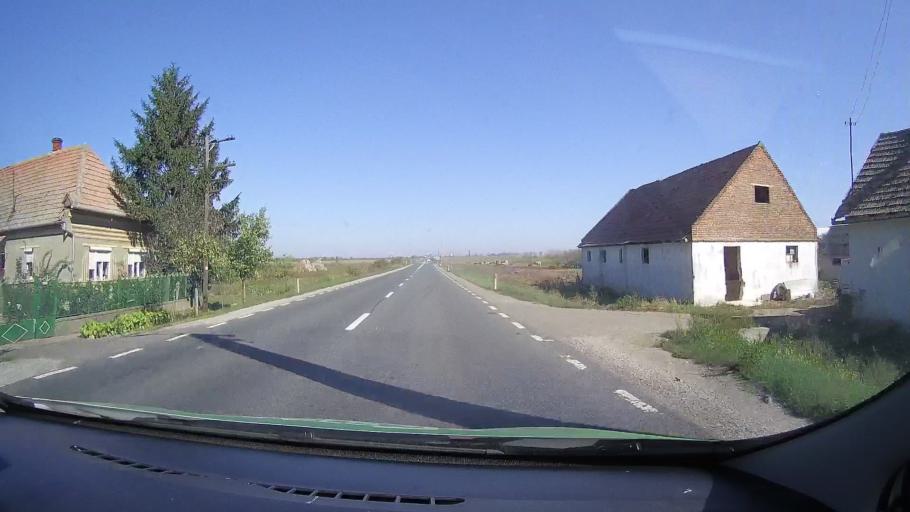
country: RO
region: Satu Mare
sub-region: Comuna Moftinu
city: Moftinu Mic
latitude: 47.6868
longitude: 22.6068
